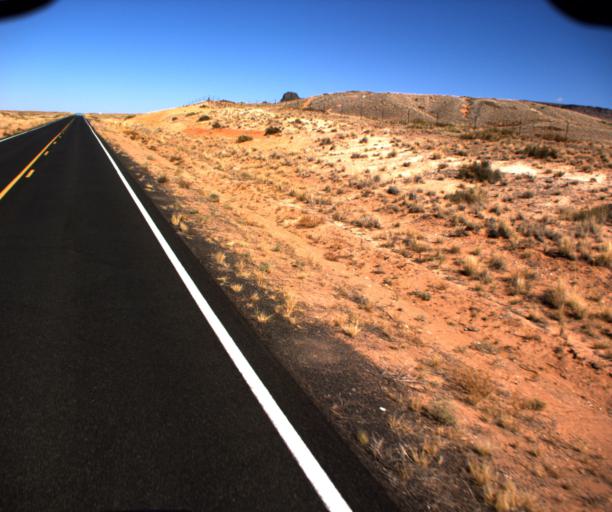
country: US
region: Arizona
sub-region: Navajo County
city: Dilkon
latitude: 35.3936
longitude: -110.4259
